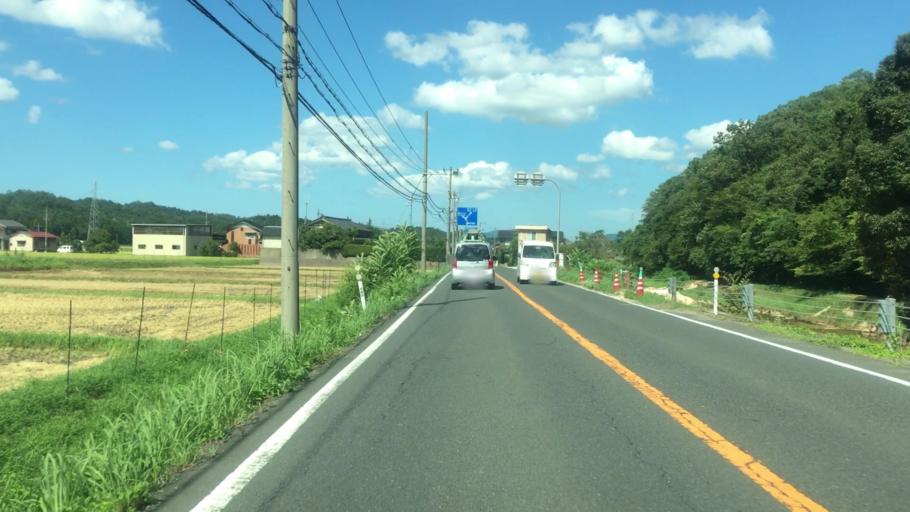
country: JP
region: Kyoto
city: Miyazu
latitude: 35.5968
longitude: 135.0443
